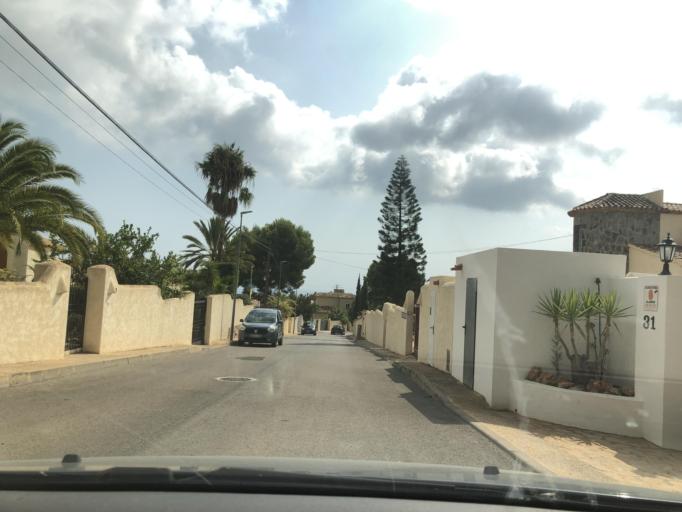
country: ES
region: Valencia
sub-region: Provincia de Alicante
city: Altea
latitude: 38.6383
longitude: -0.0668
